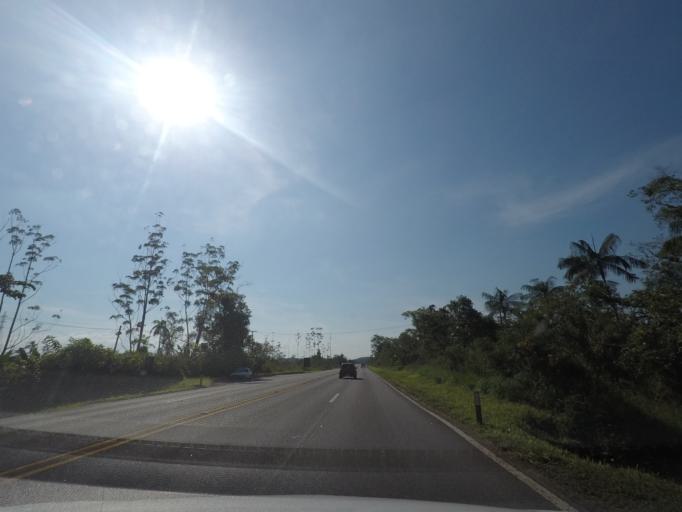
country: BR
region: Parana
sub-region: Paranagua
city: Paranagua
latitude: -25.5859
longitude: -48.6118
